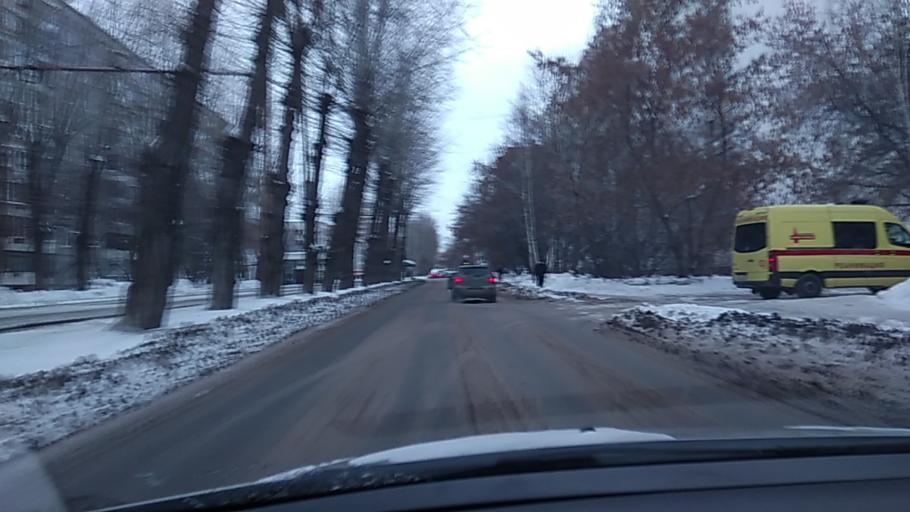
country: RU
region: Sverdlovsk
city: Yekaterinburg
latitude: 56.8219
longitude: 60.6364
